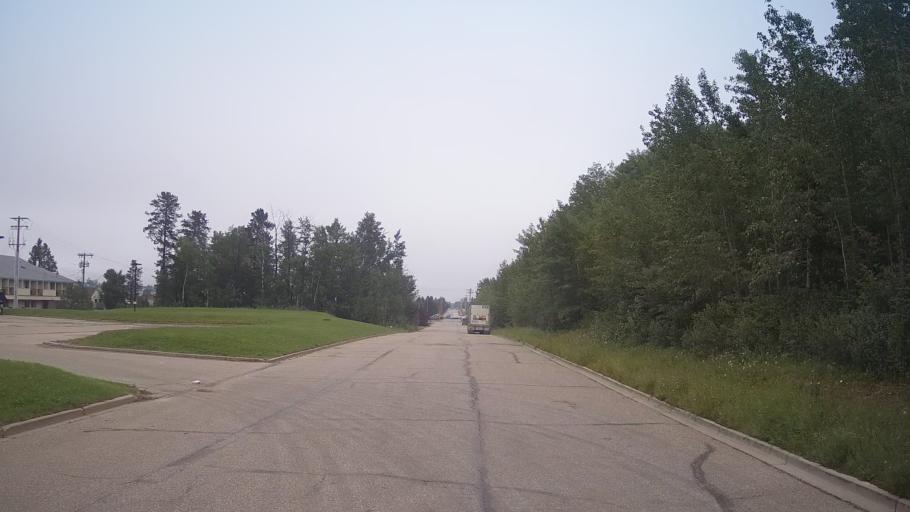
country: CA
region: Alberta
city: Edson
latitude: 53.5761
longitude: -116.4457
